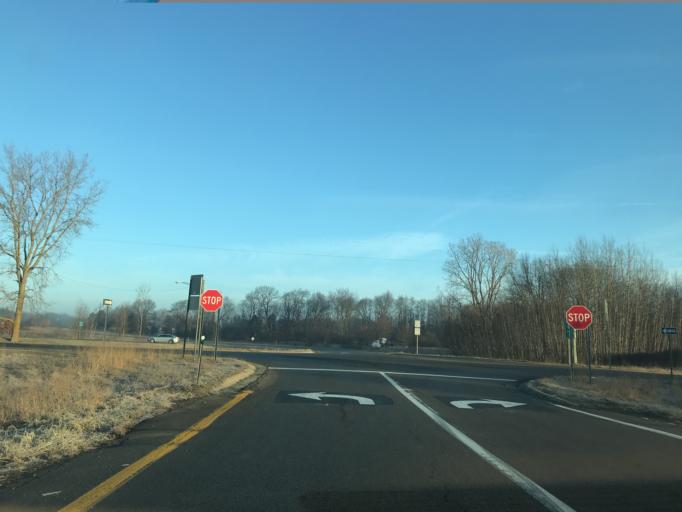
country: US
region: Michigan
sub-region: Ingham County
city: Leslie
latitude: 42.3783
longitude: -84.4266
